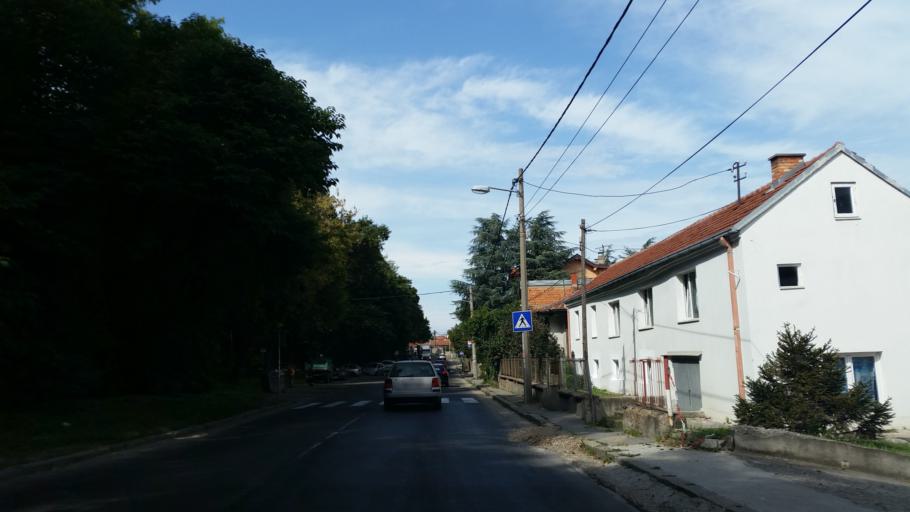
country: RS
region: Central Serbia
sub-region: Belgrade
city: Palilula
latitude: 44.8116
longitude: 20.5077
